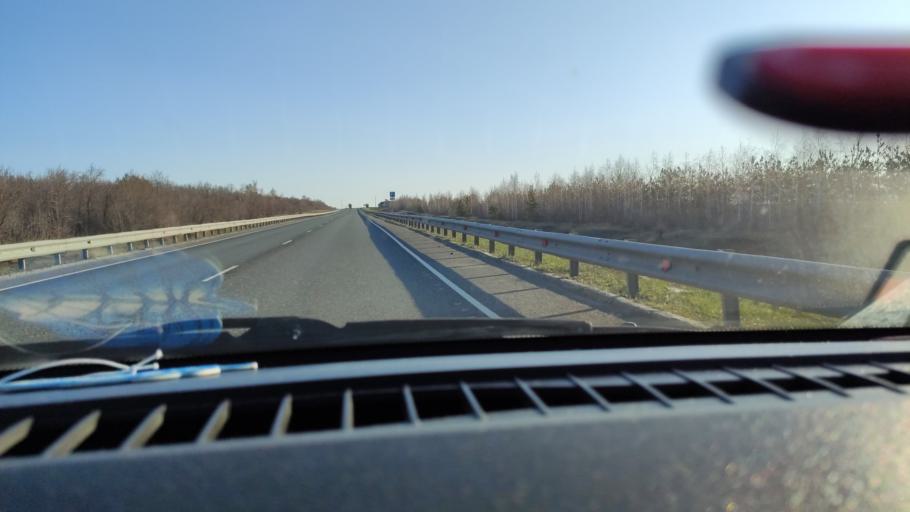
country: RU
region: Saratov
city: Balakovo
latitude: 52.1549
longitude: 47.8153
